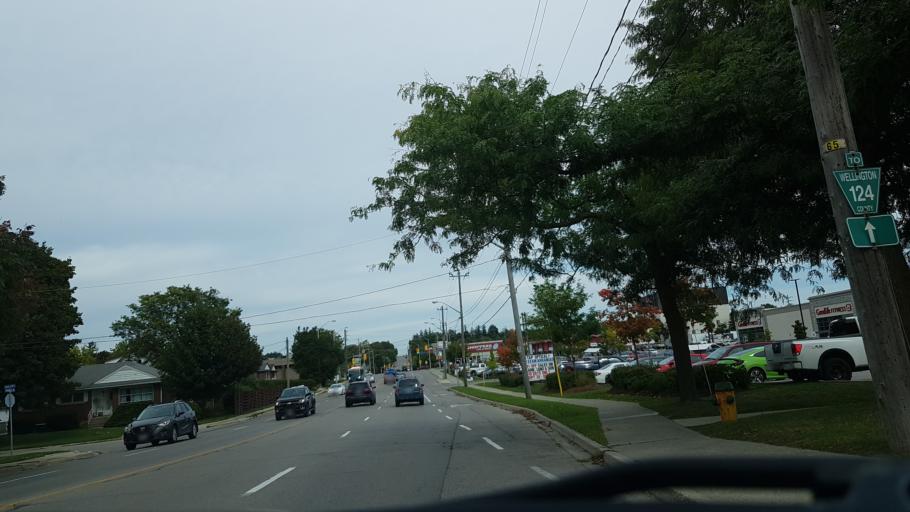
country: CA
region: Ontario
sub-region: Wellington County
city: Guelph
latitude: 43.5580
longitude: -80.2493
